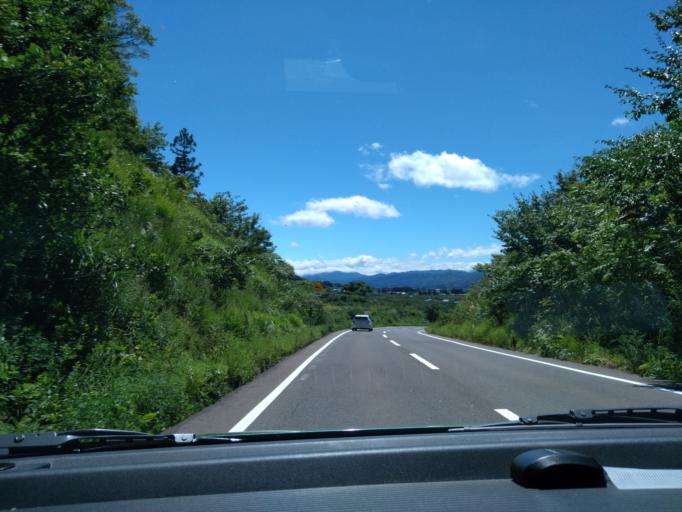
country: JP
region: Akita
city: Yokotemachi
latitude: 39.2423
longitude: 140.5631
